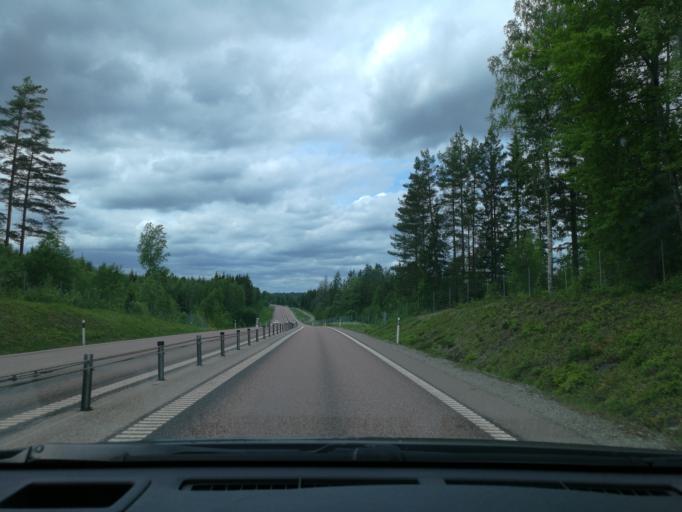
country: SE
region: Vaestmanland
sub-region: Fagersta Kommun
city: Fagersta
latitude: 59.9701
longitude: 15.8326
